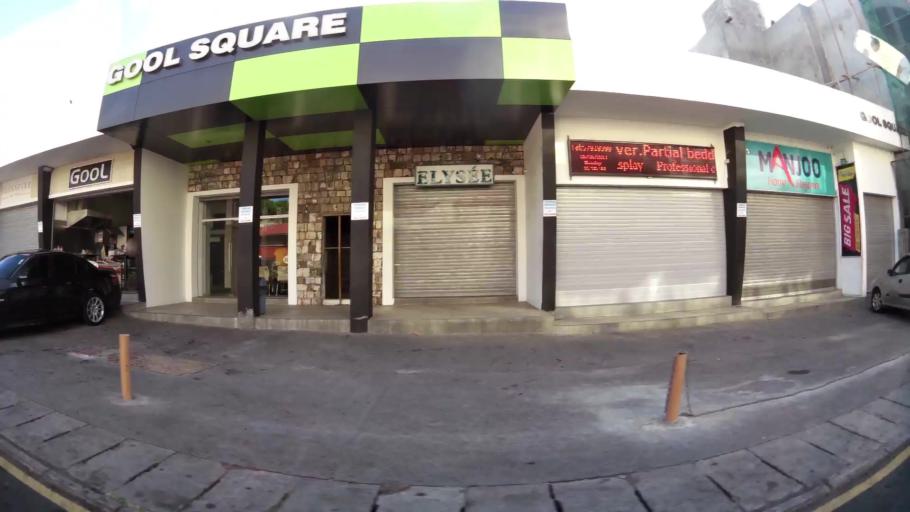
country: MU
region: Moka
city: Moka
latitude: -20.2277
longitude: 57.4677
